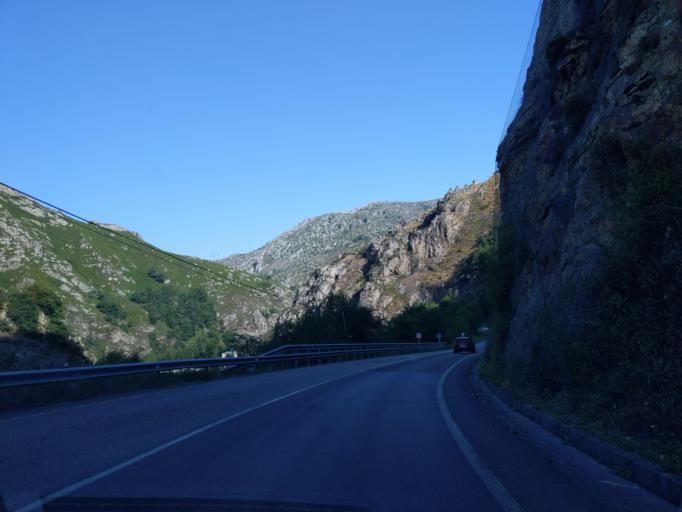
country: ES
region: Asturias
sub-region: Province of Asturias
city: Pola de Laviana
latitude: 43.2267
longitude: -5.4694
